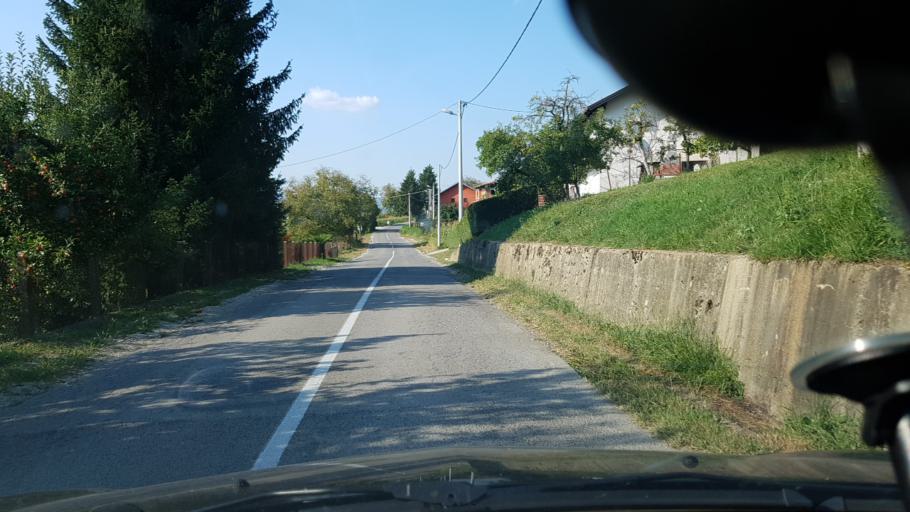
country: HR
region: Zagrebacka
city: Pojatno
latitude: 45.9252
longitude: 15.7175
